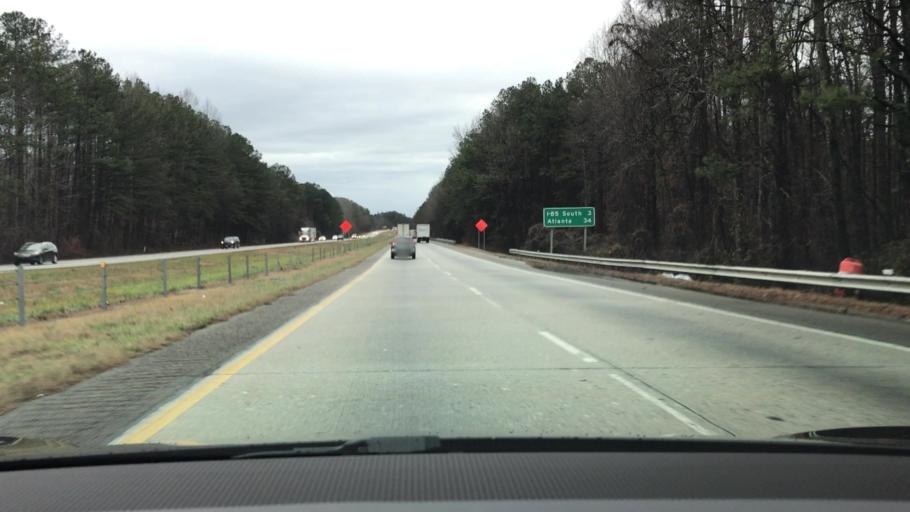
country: US
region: Georgia
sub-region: Gwinnett County
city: Sugar Hill
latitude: 34.0757
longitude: -84.0021
